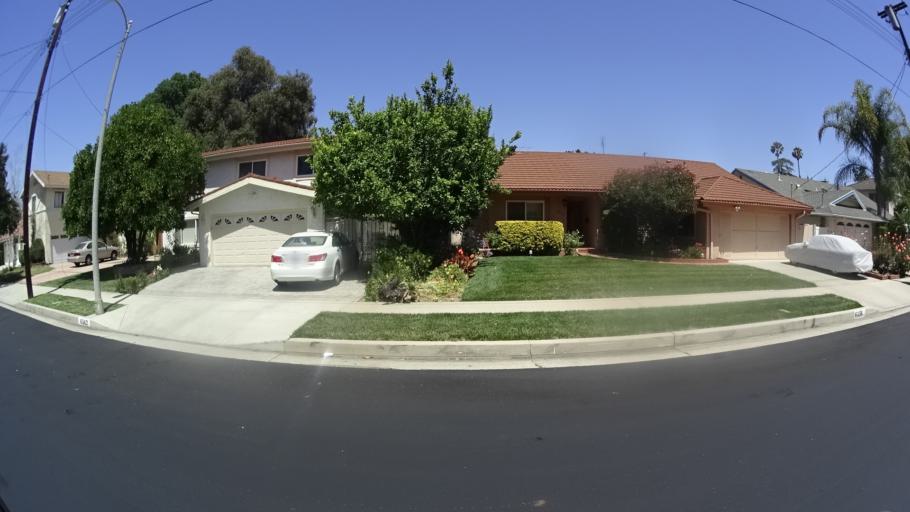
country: US
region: California
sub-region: Los Angeles County
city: Northridge
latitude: 34.1903
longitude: -118.5131
